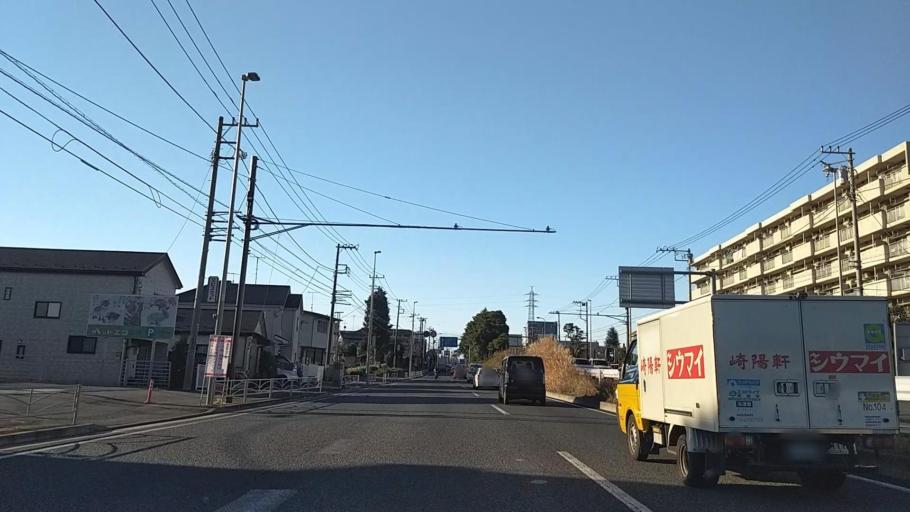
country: JP
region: Kanagawa
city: Fujisawa
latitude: 35.3752
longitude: 139.5041
